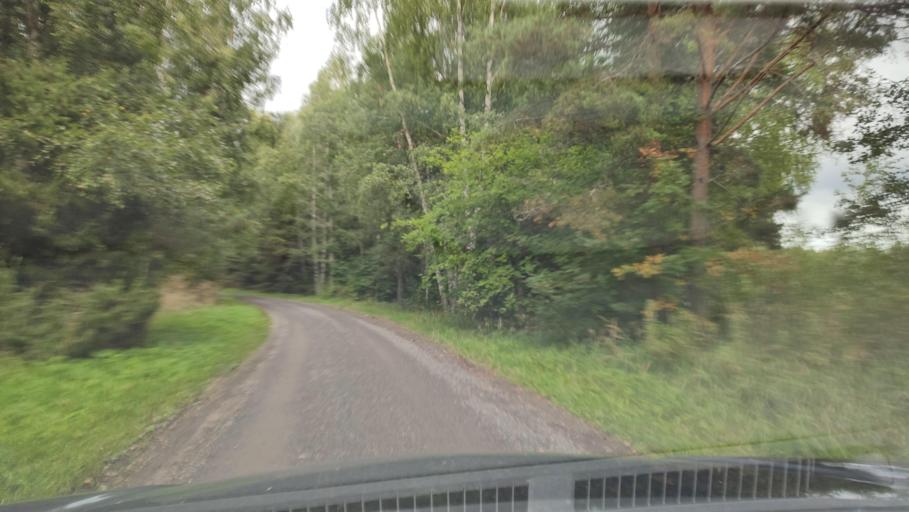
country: FI
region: Ostrobothnia
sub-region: Sydosterbotten
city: Kristinestad
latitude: 62.2480
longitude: 21.3232
